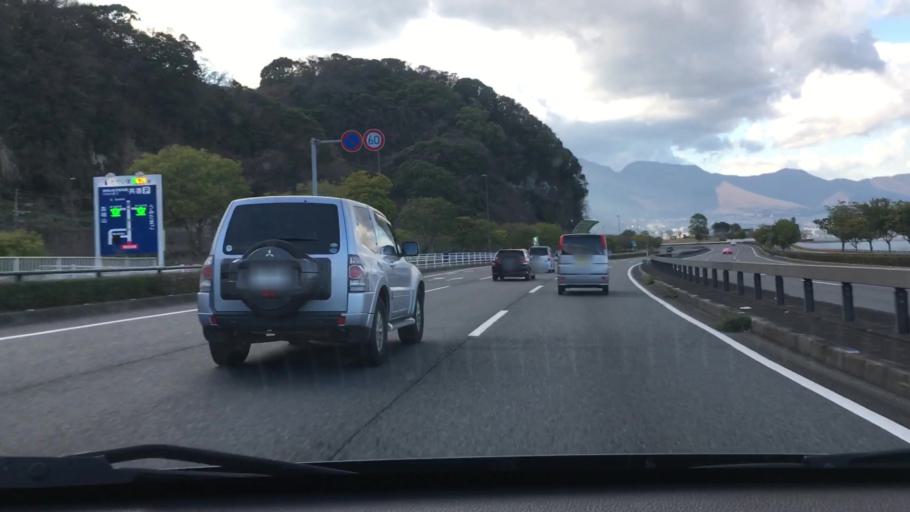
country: JP
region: Oita
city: Oita
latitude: 33.2559
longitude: 131.5569
